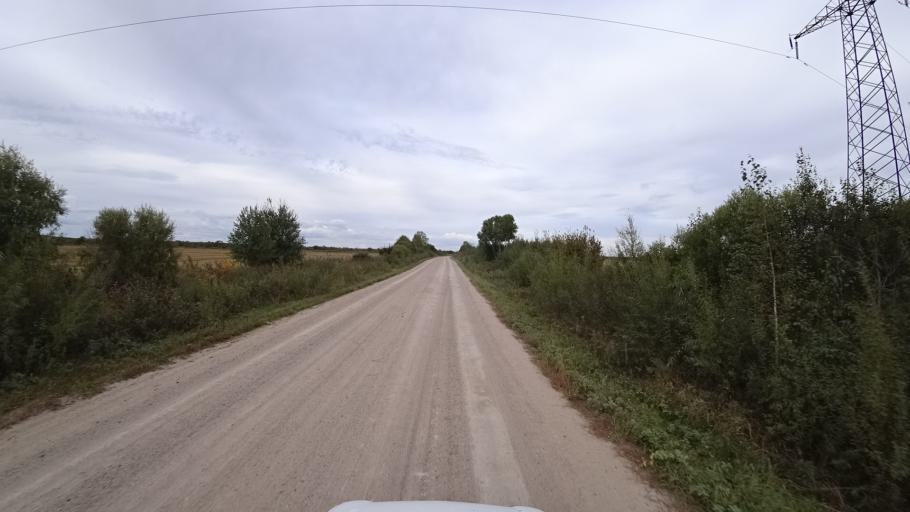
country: RU
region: Amur
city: Arkhara
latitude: 49.3735
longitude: 130.1487
